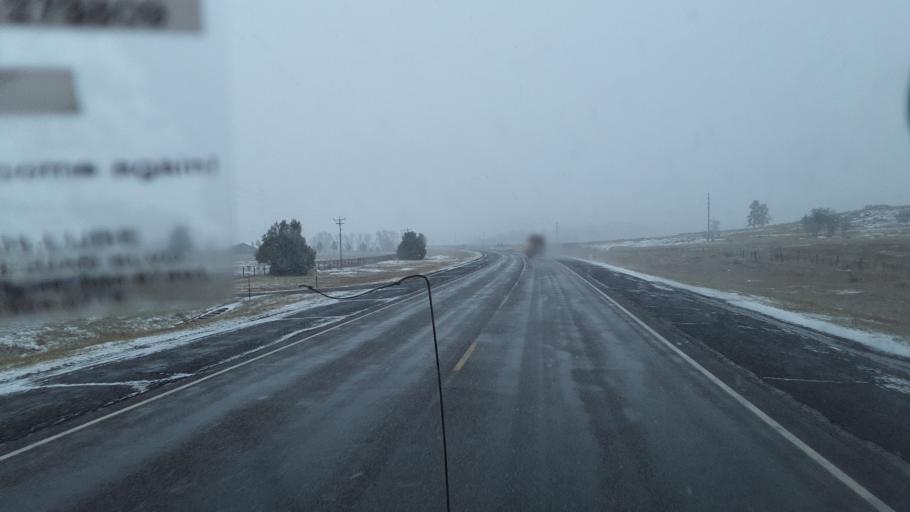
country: US
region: New Mexico
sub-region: Rio Arriba County
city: Chama
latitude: 36.8377
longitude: -106.5691
